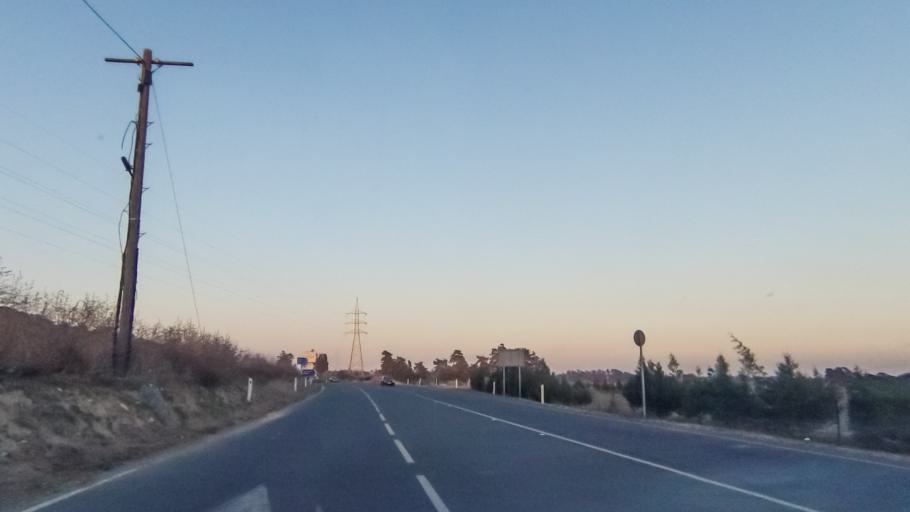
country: CY
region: Limassol
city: Erimi
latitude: 34.6639
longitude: 32.8963
